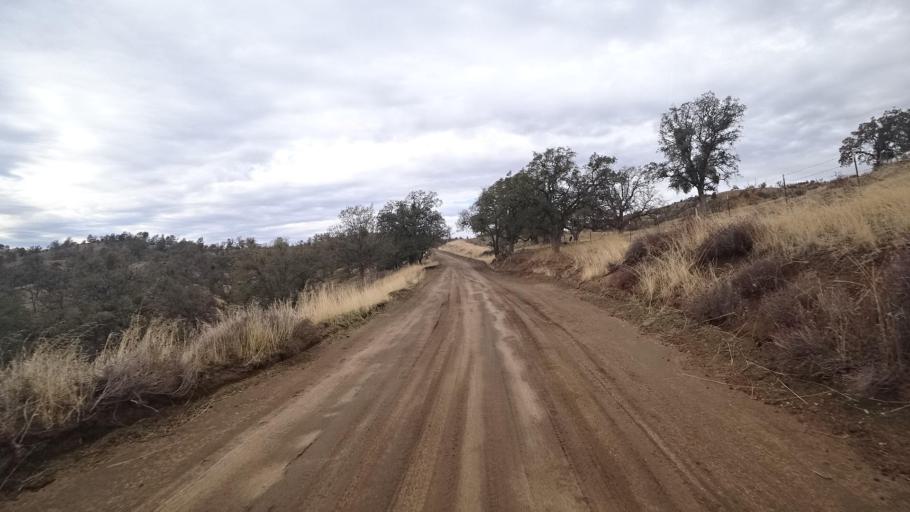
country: US
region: California
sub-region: Kern County
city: Stallion Springs
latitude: 35.1171
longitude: -118.6961
